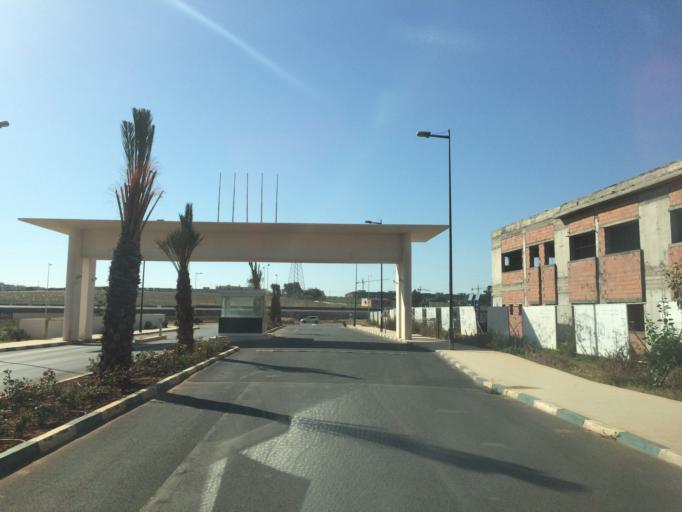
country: MA
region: Rabat-Sale-Zemmour-Zaer
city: Sale
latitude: 33.9872
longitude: -6.7266
